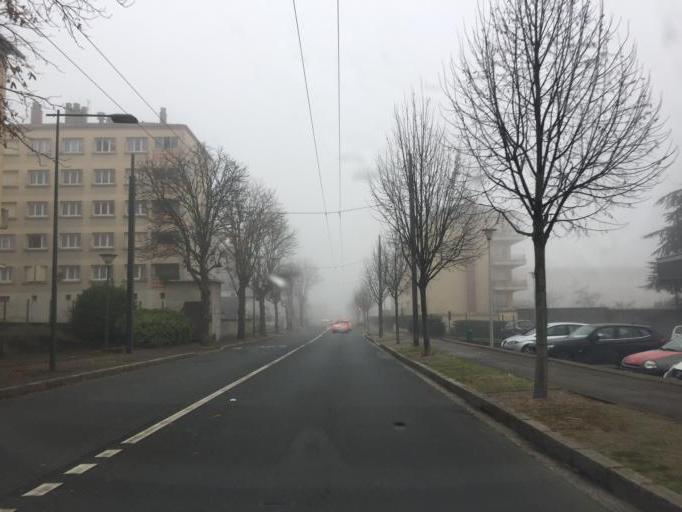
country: FR
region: Rhone-Alpes
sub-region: Departement du Rhone
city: Caluire-et-Cuire
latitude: 45.7930
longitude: 4.8451
